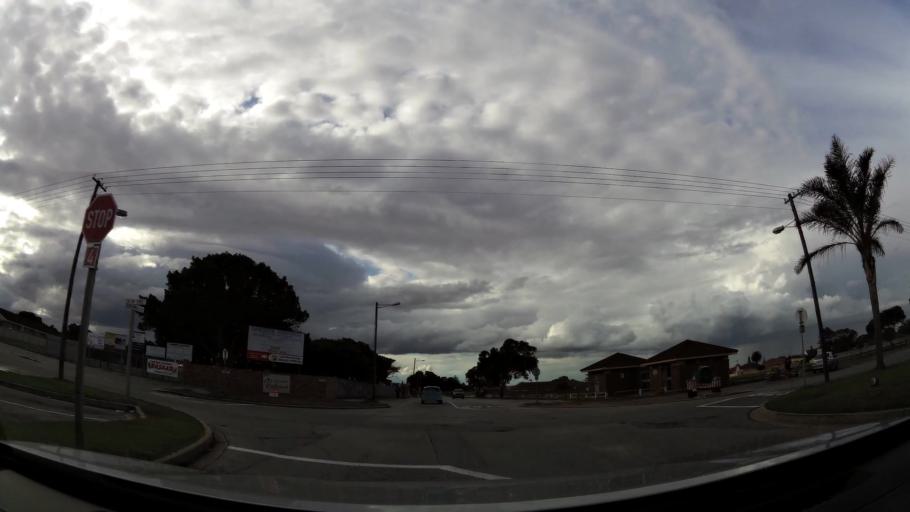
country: ZA
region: Eastern Cape
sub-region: Nelson Mandela Bay Metropolitan Municipality
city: Port Elizabeth
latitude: -33.9431
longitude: 25.5144
